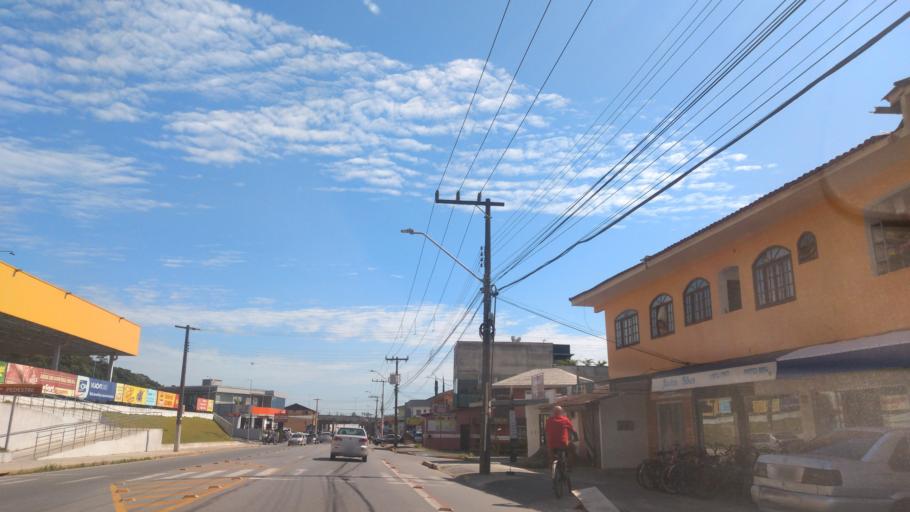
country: BR
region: Santa Catarina
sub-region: Joinville
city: Joinville
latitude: -26.2379
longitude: -48.8182
